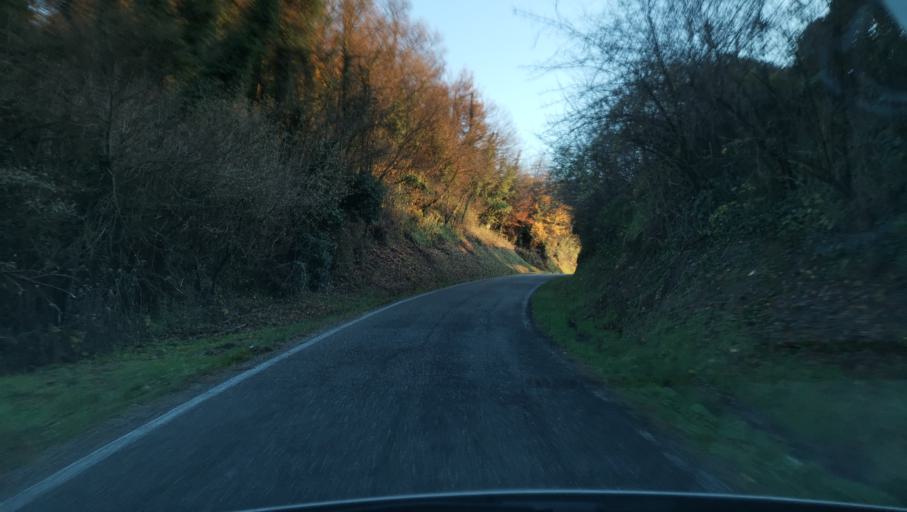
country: IT
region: Piedmont
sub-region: Provincia di Asti
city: Moncucco Torinese
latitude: 45.0807
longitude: 7.9267
